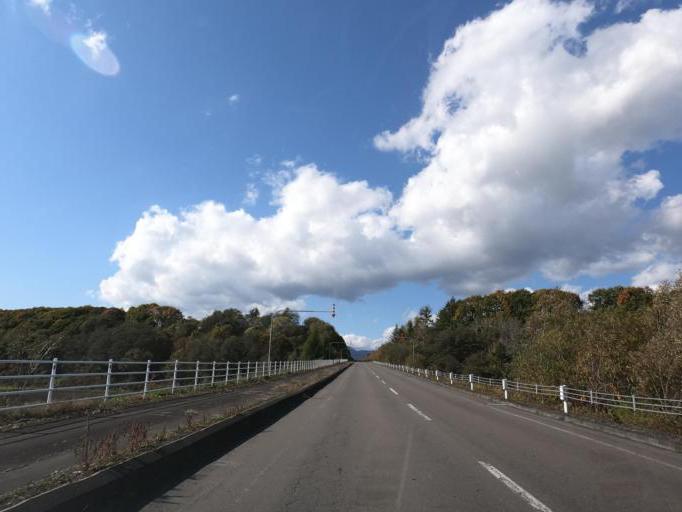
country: JP
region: Hokkaido
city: Otofuke
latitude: 43.2390
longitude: 143.2679
